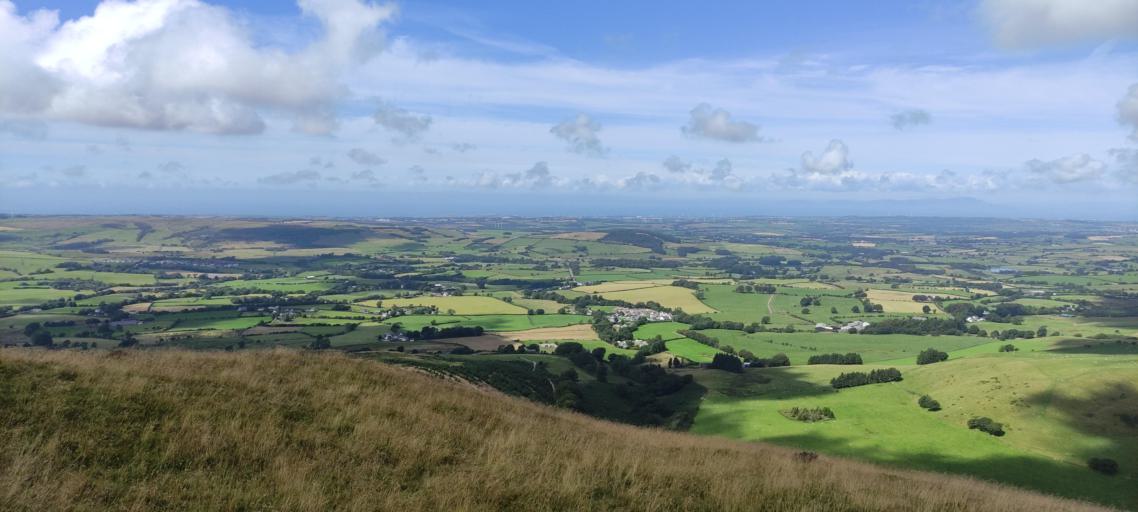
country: GB
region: England
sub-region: Cumbria
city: Frizington
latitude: 54.5588
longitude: -3.4013
